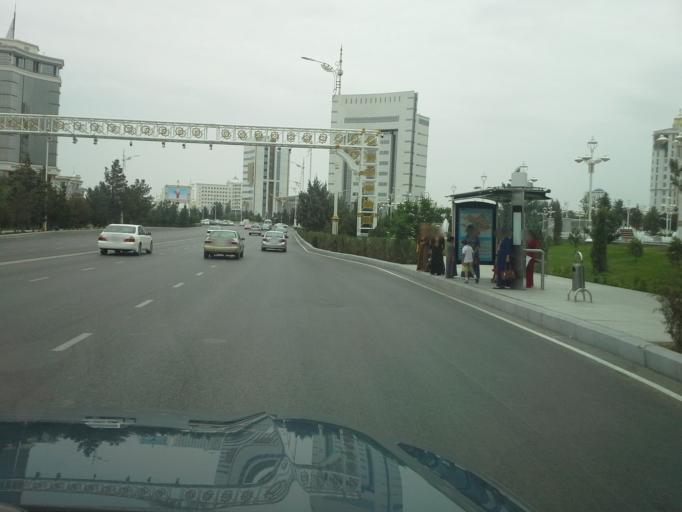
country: TM
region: Ahal
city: Ashgabat
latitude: 37.9261
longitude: 58.3740
